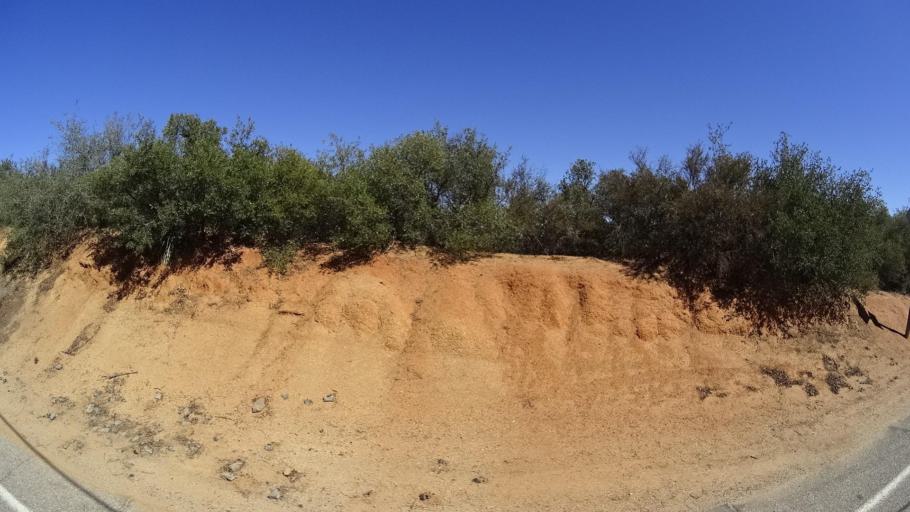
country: US
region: California
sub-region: San Diego County
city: Jamul
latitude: 32.7260
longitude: -116.7691
